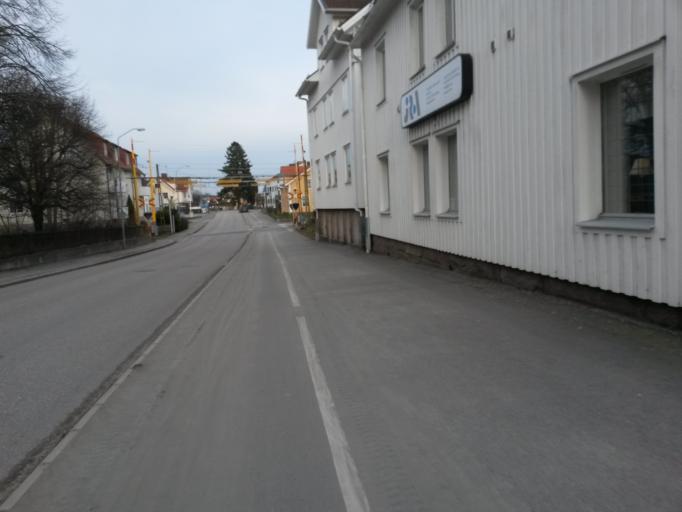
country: SE
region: Vaestra Goetaland
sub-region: Herrljunga Kommun
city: Herrljunga
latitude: 58.0784
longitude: 13.0289
